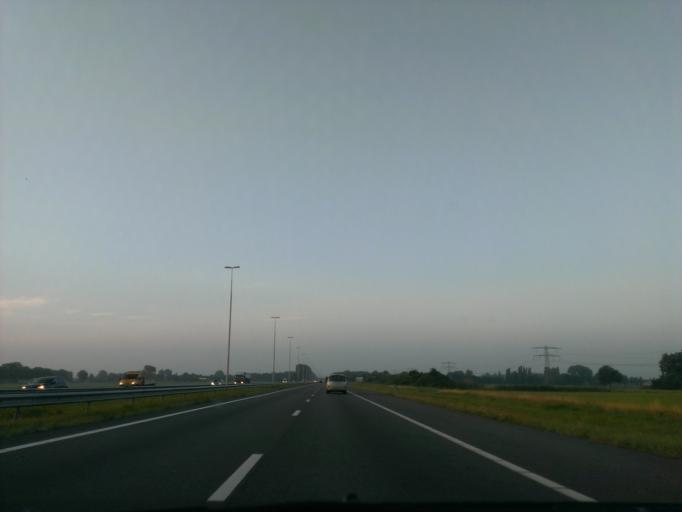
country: NL
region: Gelderland
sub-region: Gemeente Apeldoorn
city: Apeldoorn
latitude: 52.2459
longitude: 6.0082
